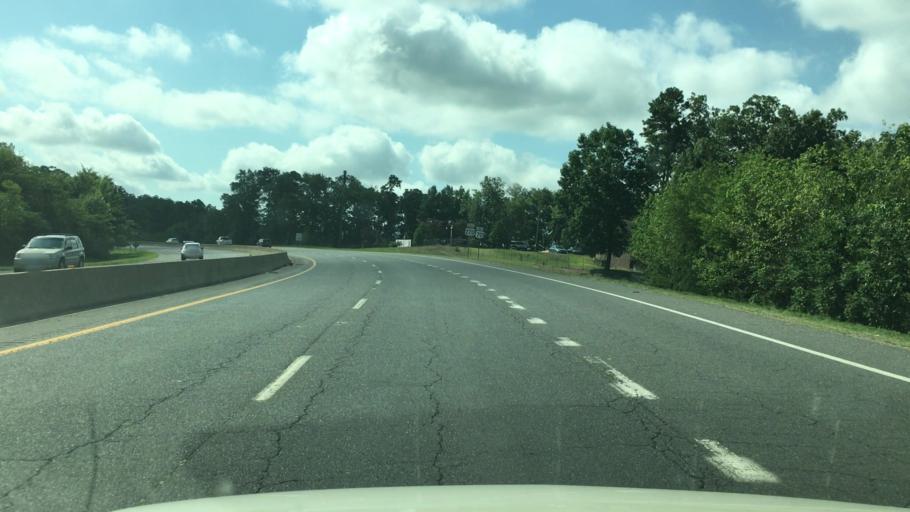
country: US
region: Arkansas
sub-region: Garland County
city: Lake Hamilton
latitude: 34.4675
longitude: -93.0877
